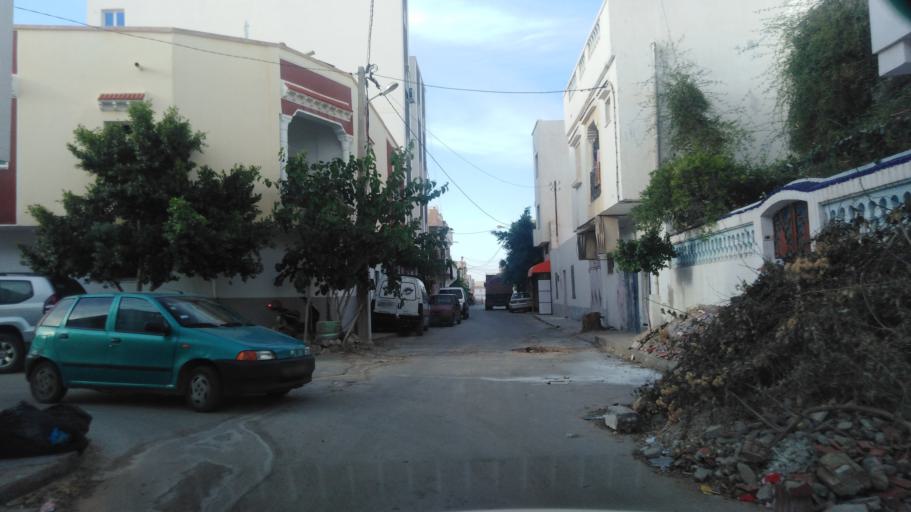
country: TN
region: Tataouine
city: Tataouine
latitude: 32.9346
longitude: 10.4524
